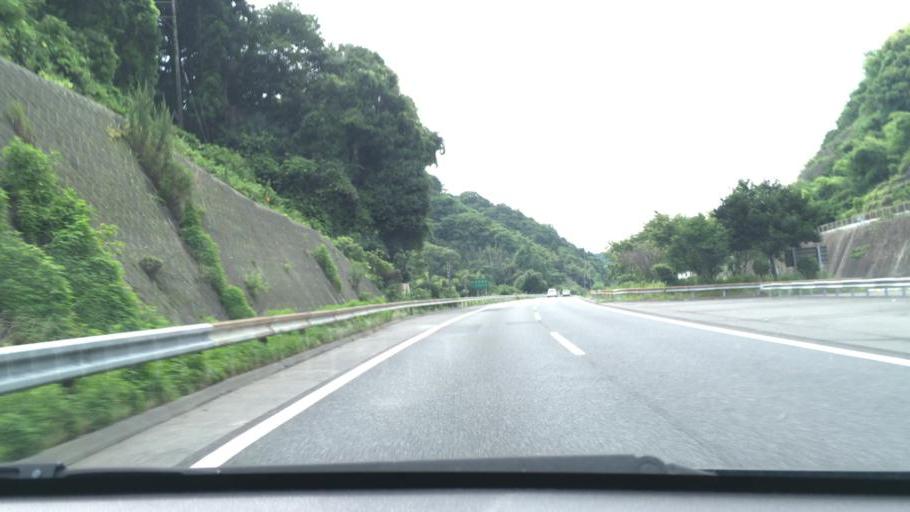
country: JP
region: Yamaguchi
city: Tokuyama
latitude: 34.0733
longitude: 131.8074
